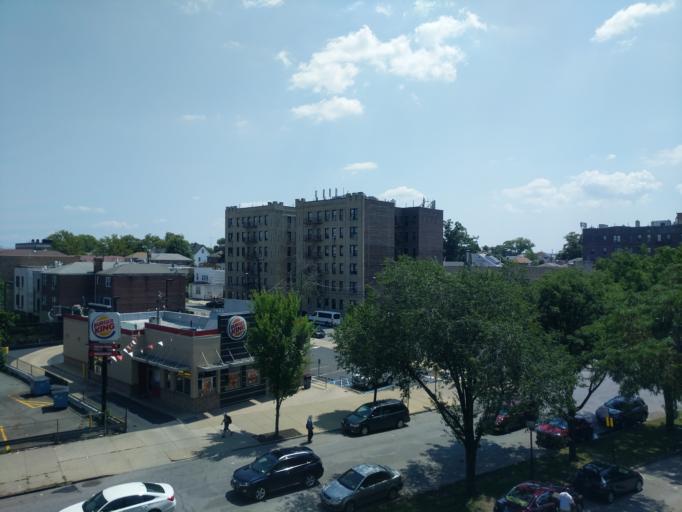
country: US
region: New York
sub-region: Bronx
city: The Bronx
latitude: 40.8432
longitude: -73.8371
